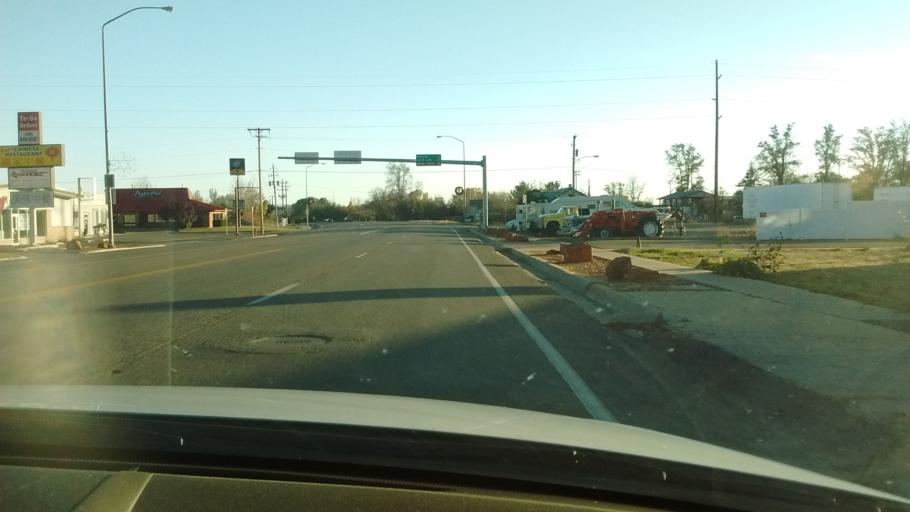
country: US
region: Utah
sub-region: Kane County
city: Kanab
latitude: 37.0421
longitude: -112.5265
